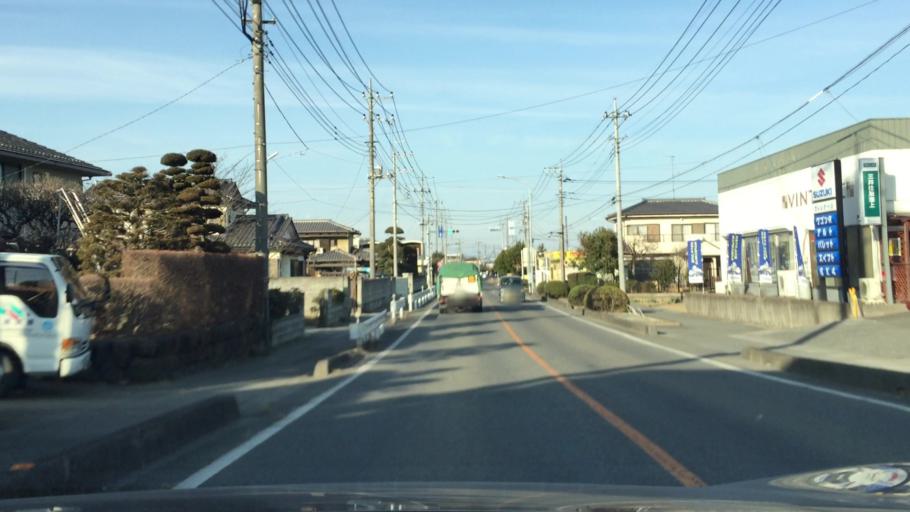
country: JP
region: Saitama
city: Menuma
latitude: 36.2071
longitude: 139.3759
